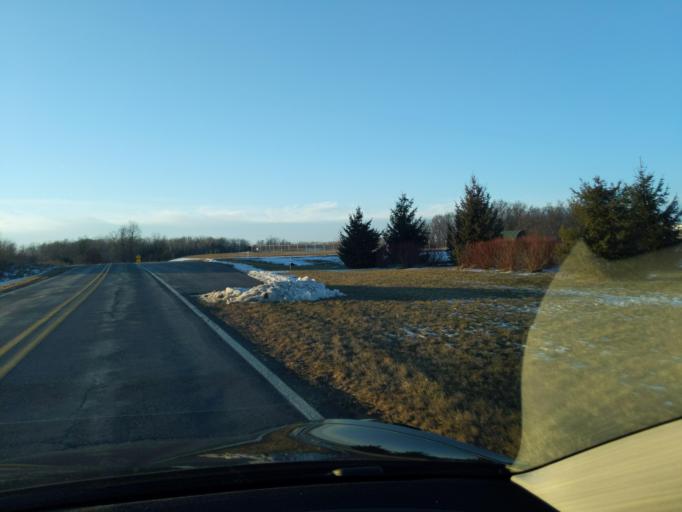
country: US
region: Michigan
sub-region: Ingham County
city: Stockbridge
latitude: 42.5024
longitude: -84.2368
